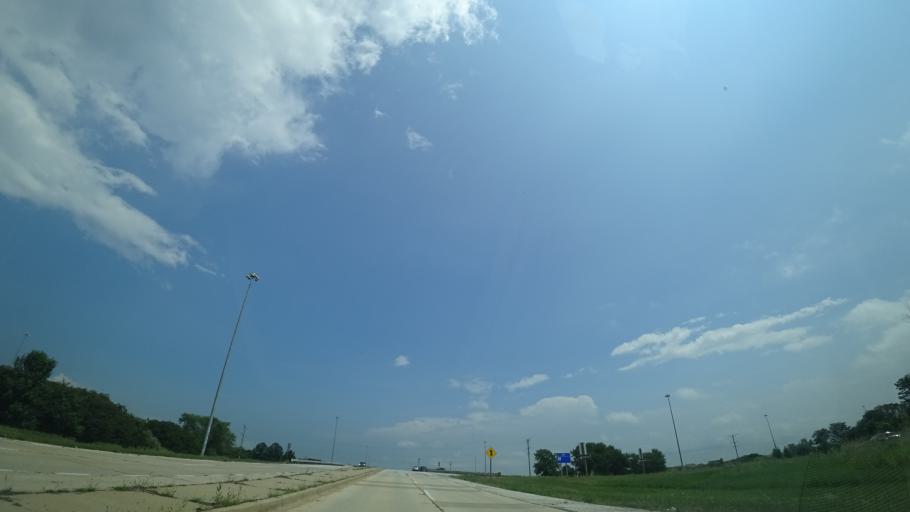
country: US
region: Illinois
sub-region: Cook County
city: Matteson
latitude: 41.5280
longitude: -87.7449
